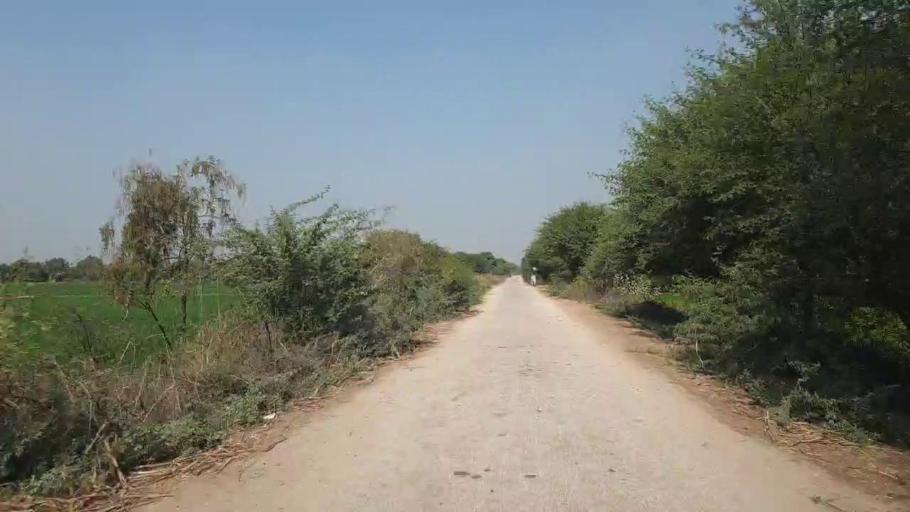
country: PK
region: Sindh
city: Chambar
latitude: 25.4064
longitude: 68.8878
